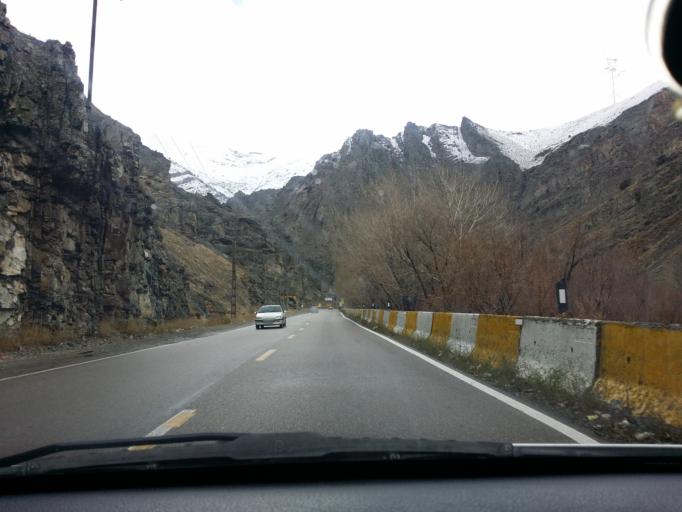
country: IR
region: Tehran
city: Tajrish
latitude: 36.0144
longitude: 51.2872
